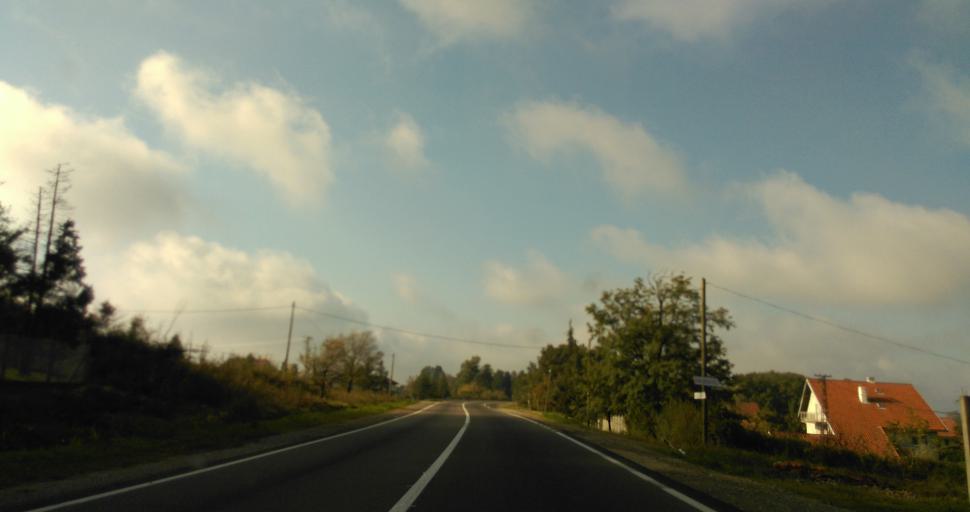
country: RS
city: Vranic
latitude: 44.5897
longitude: 20.3436
